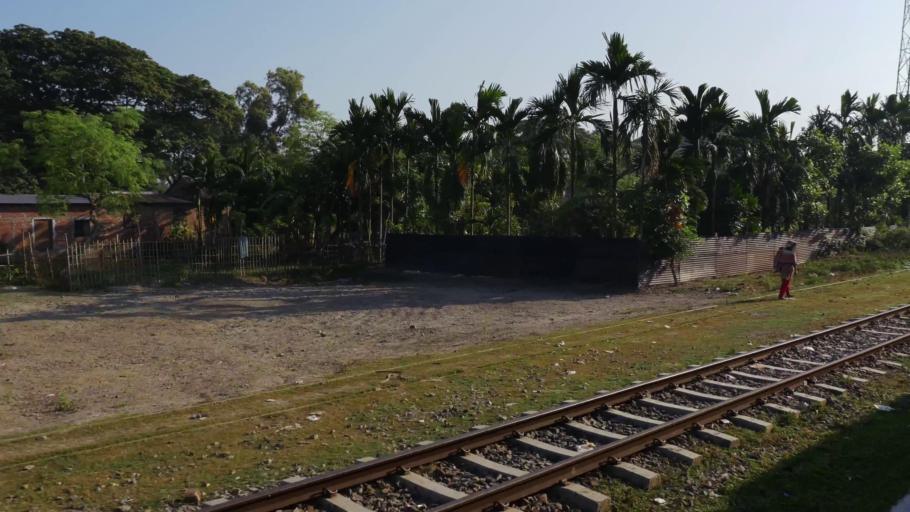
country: BD
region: Dhaka
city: Jamalpur
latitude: 24.8641
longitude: 90.1132
